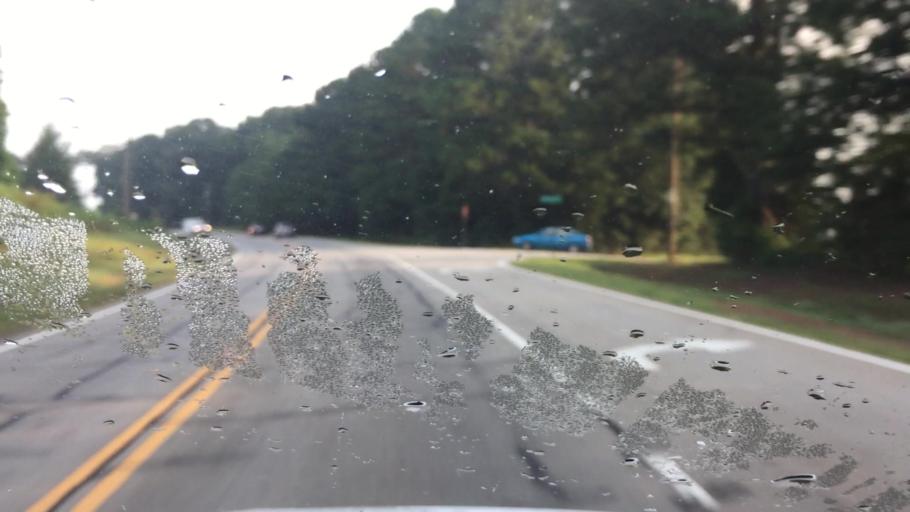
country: US
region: Georgia
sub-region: Henry County
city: Stockbridge
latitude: 33.5628
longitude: -84.1376
